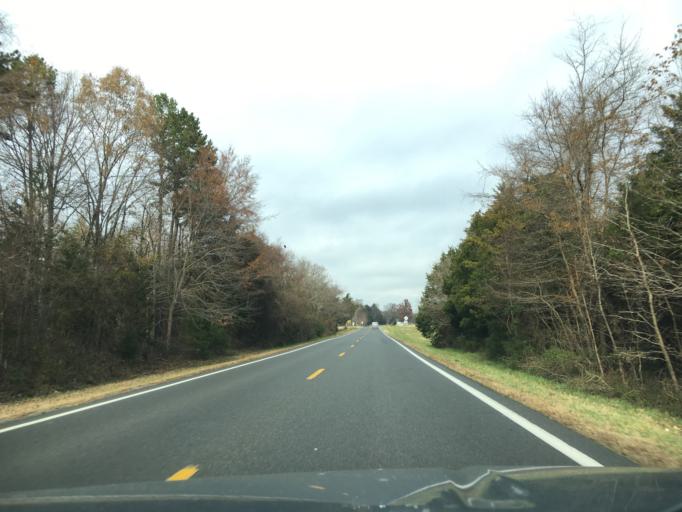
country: US
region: Virginia
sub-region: Prince Edward County
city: Farmville
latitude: 37.3547
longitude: -78.3803
